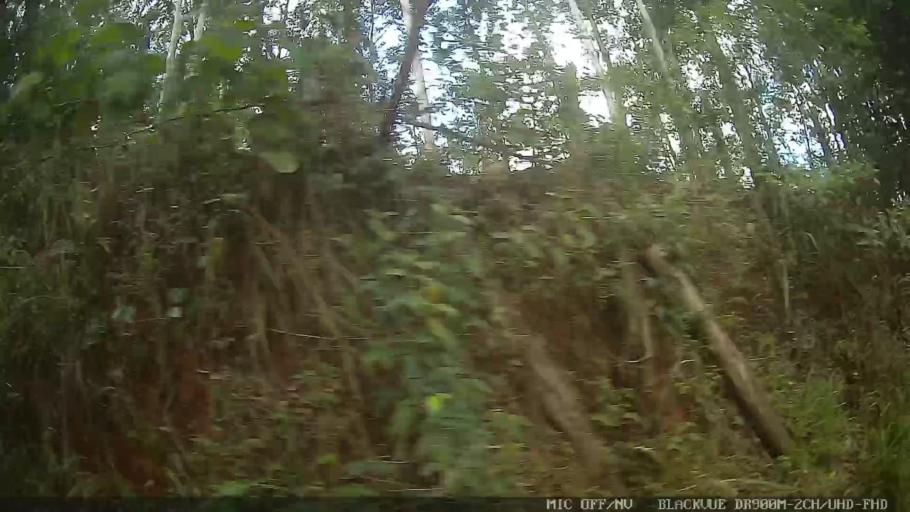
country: BR
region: Sao Paulo
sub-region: Braganca Paulista
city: Braganca Paulista
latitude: -23.0247
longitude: -46.4669
